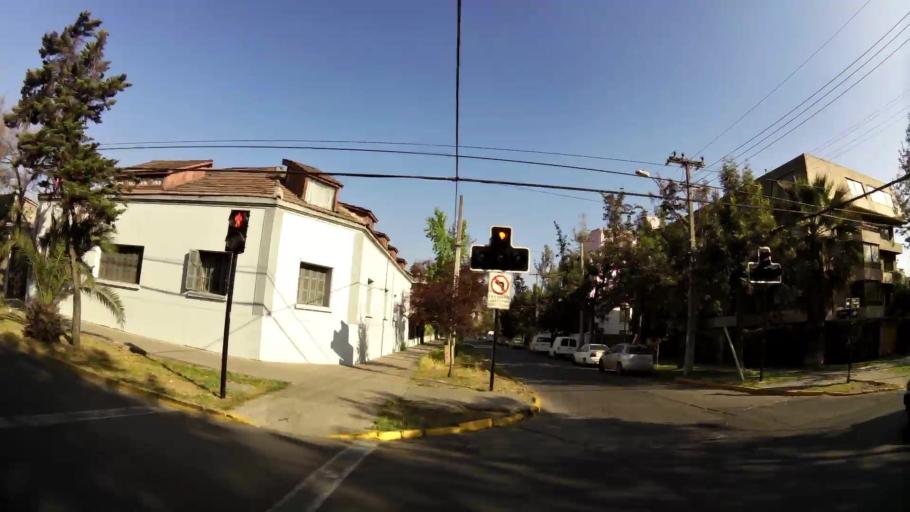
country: CL
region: Santiago Metropolitan
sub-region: Provincia de Santiago
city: Villa Presidente Frei, Nunoa, Santiago, Chile
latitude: -33.4452
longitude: -70.6043
